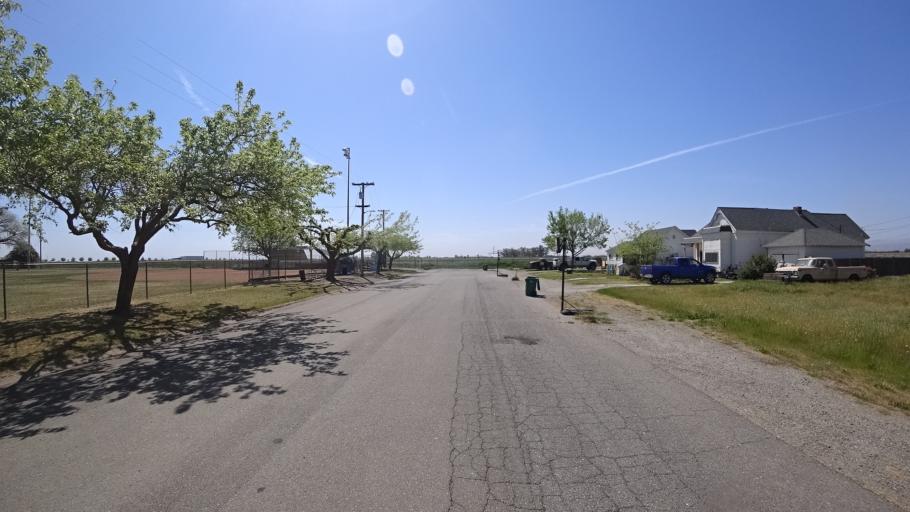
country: US
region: California
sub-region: Glenn County
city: Willows
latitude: 39.5123
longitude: -122.2031
